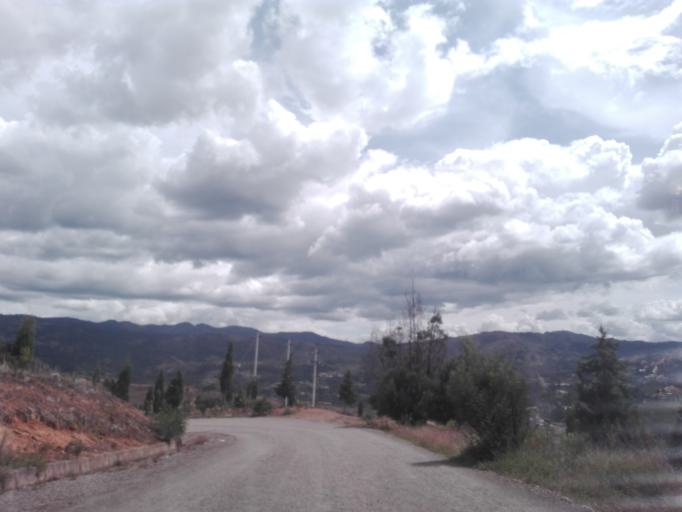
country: CO
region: Boyaca
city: Raquira
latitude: 5.5439
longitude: -73.6222
